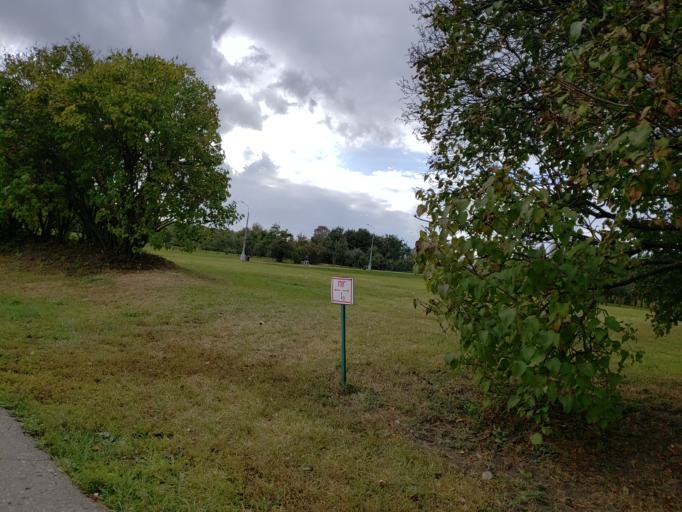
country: RU
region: Moscow
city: Kolomenskoye
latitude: 55.6723
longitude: 37.6742
